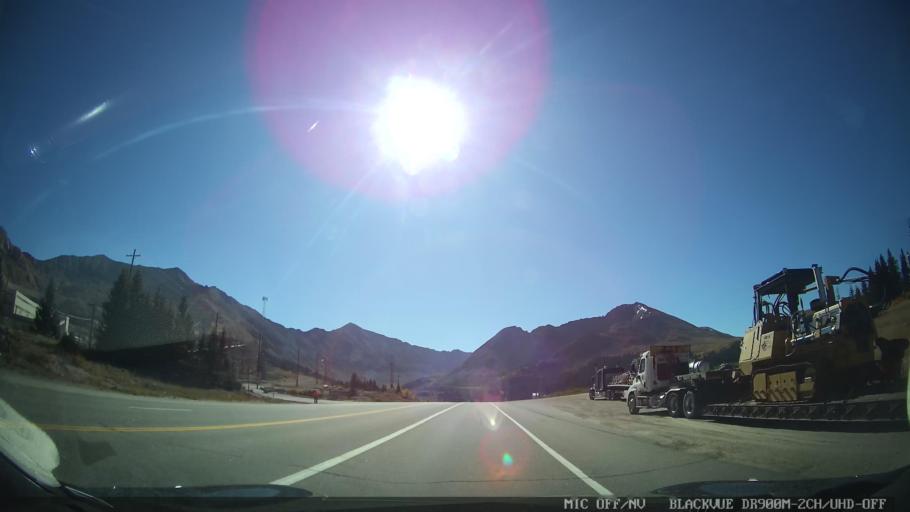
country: US
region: Colorado
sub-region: Lake County
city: Leadville
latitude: 39.3688
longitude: -106.1888
